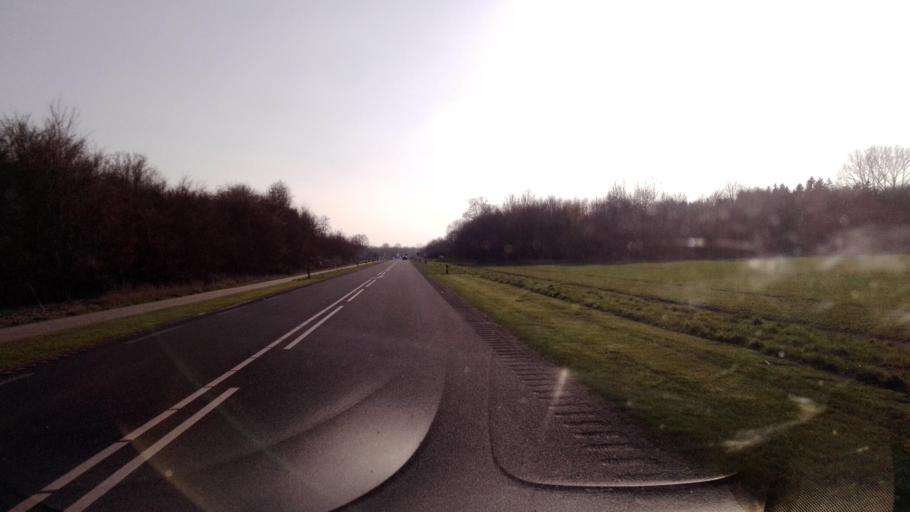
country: NL
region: Gelderland
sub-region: Gemeente Elburg
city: Elburg
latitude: 52.4506
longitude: 5.7965
